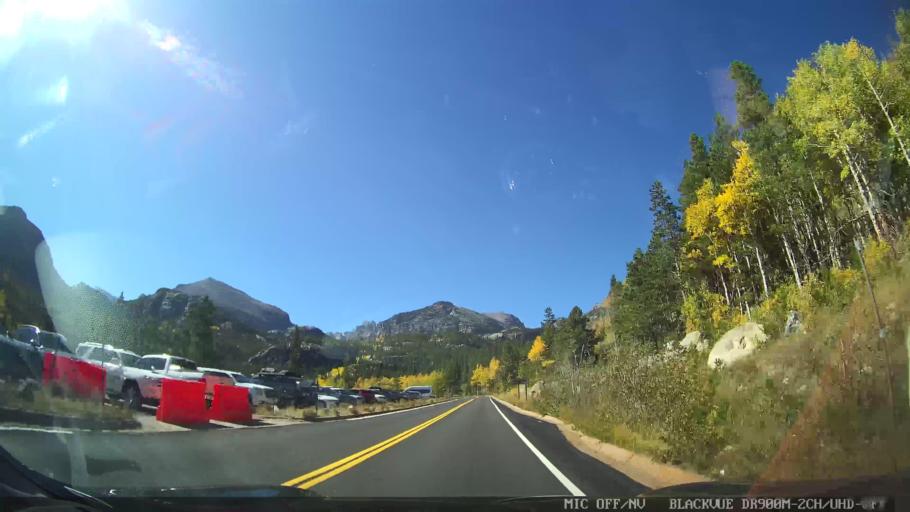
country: US
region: Colorado
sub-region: Larimer County
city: Estes Park
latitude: 40.3113
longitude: -105.6394
